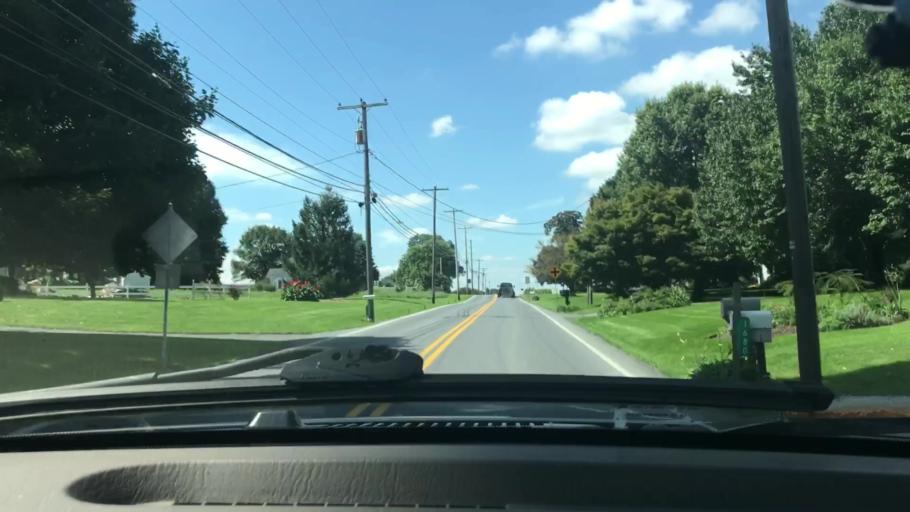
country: US
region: Pennsylvania
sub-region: Lancaster County
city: Landisville
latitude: 40.1142
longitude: -76.3843
